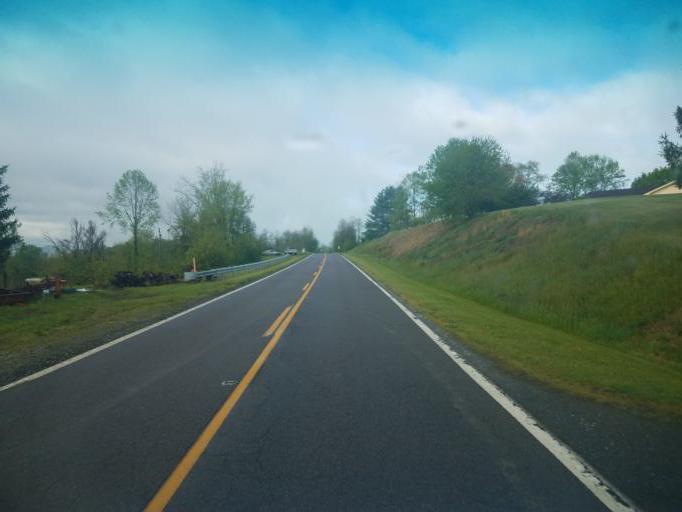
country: US
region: Virginia
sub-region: Washington County
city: Emory
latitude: 36.7034
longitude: -81.7880
